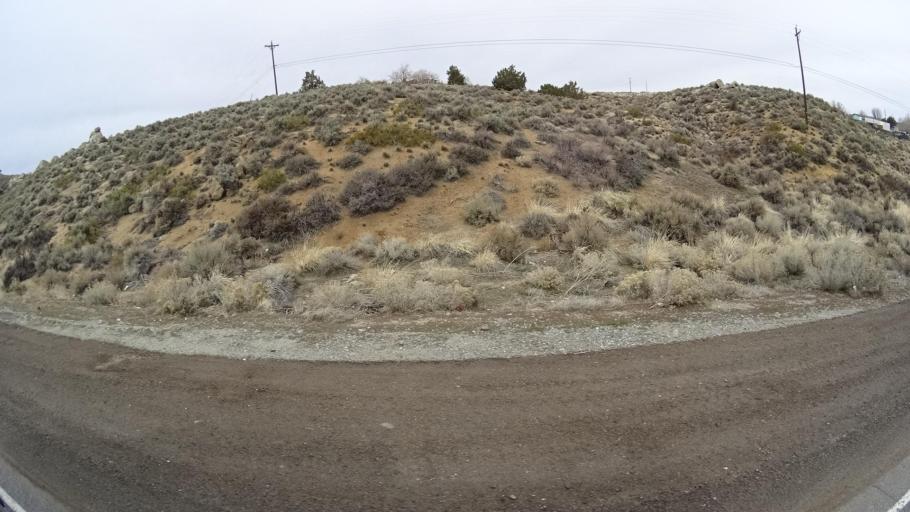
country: US
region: Nevada
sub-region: Washoe County
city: Sun Valley
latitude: 39.6009
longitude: -119.7989
